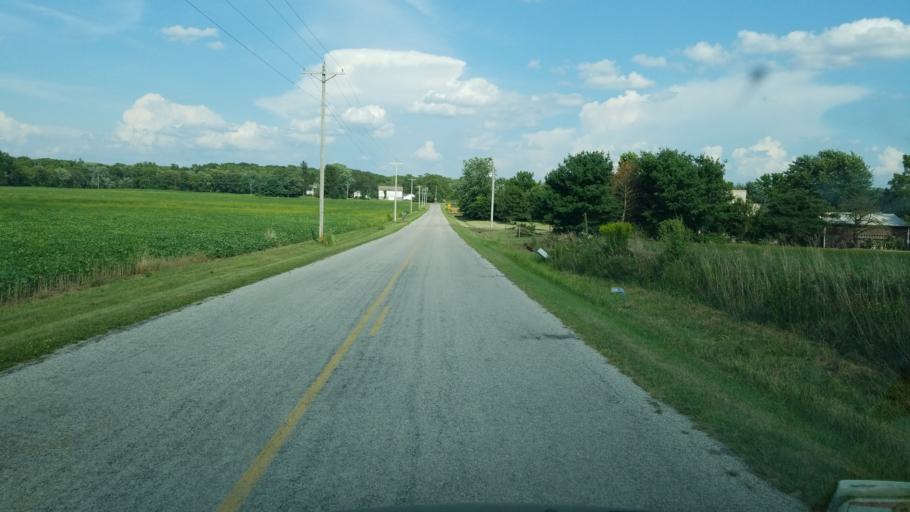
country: US
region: Ohio
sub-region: Marion County
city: Prospect
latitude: 40.4946
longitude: -83.2018
